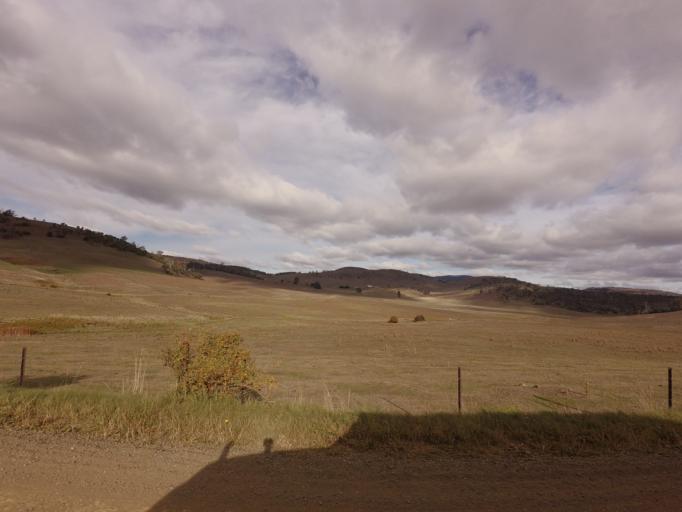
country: AU
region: Tasmania
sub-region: Brighton
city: Bridgewater
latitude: -42.4609
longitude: 147.2756
